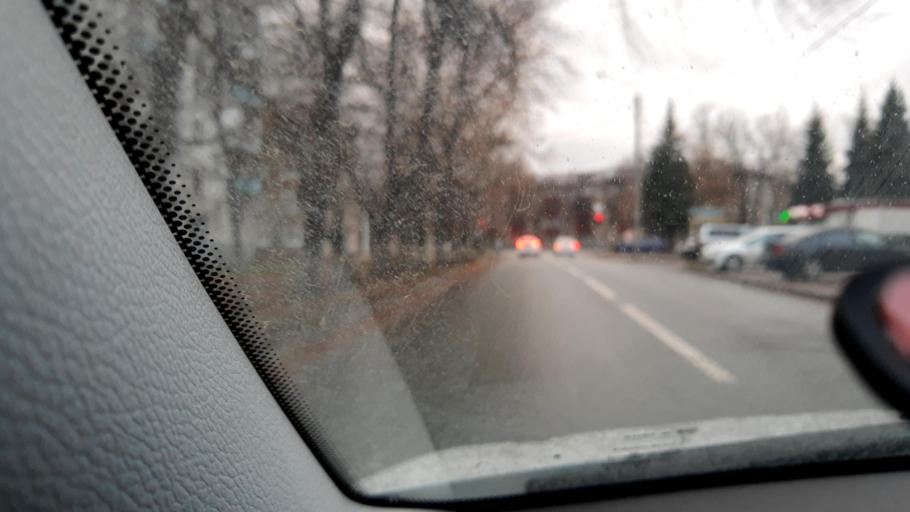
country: RU
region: Bashkortostan
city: Ufa
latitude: 54.8181
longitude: 56.1087
